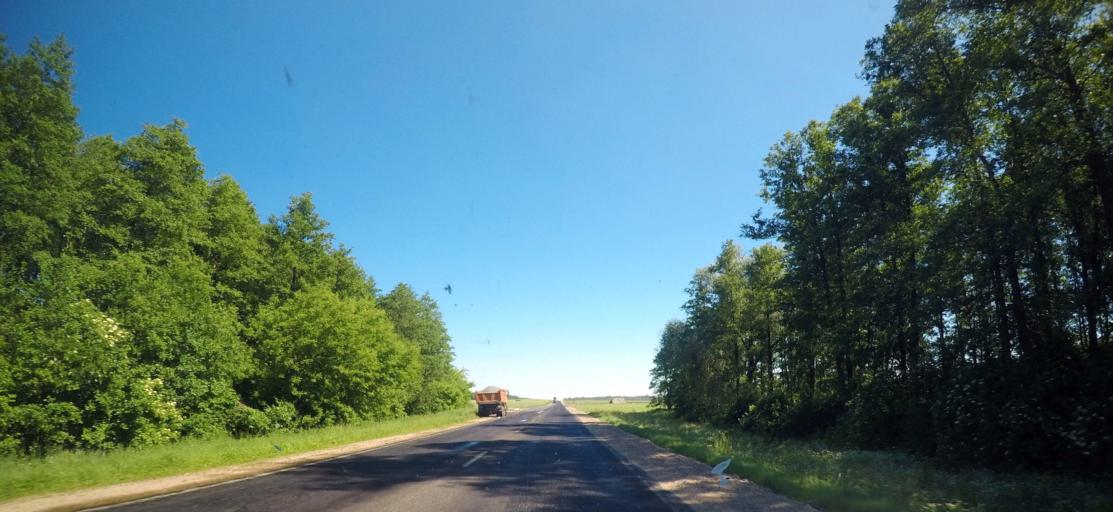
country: BY
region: Grodnenskaya
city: Vyalikaya Byerastavitsa
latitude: 53.2287
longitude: 23.9899
